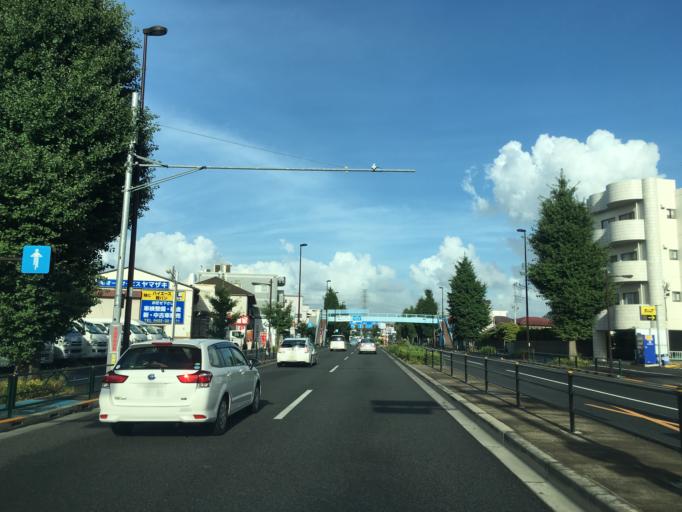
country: JP
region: Tokyo
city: Mitaka-shi
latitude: 35.6814
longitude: 139.5356
